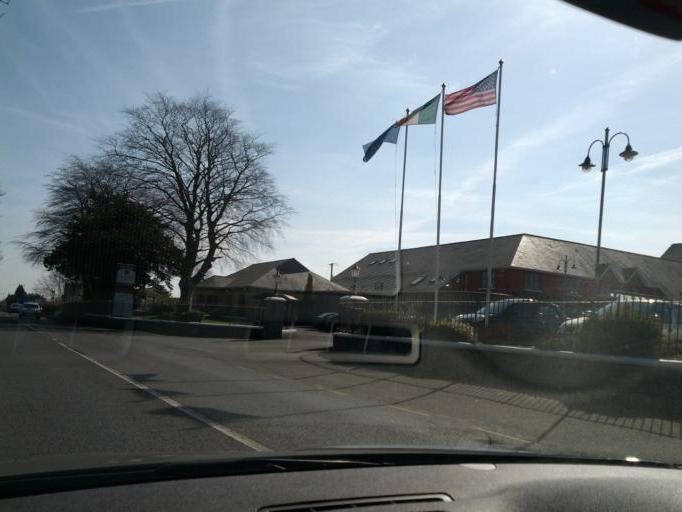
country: IE
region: Leinster
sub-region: Kildare
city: Leixlip
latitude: 53.3610
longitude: -6.4800
